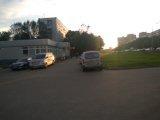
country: RU
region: Moscow
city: Chertanovo Yuzhnoye
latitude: 55.6114
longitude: 37.5987
